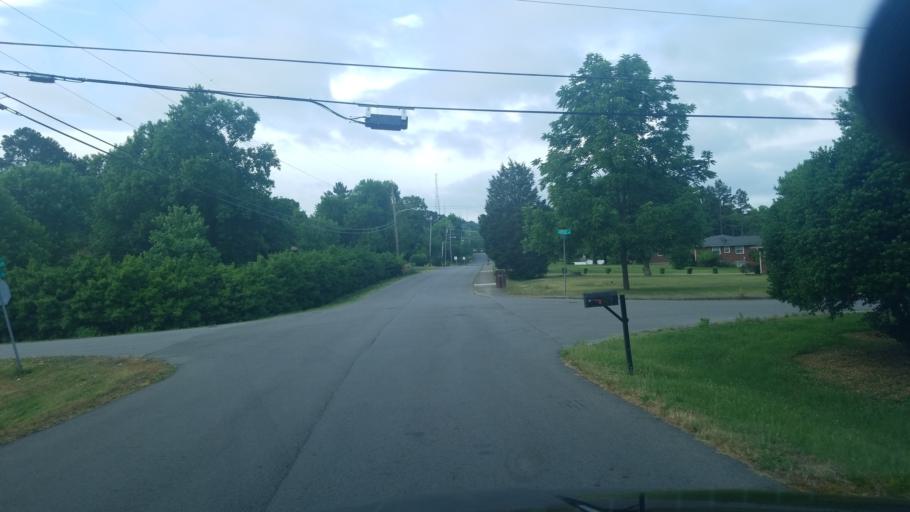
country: US
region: Tennessee
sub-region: Davidson County
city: Nashville
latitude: 36.2326
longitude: -86.7436
